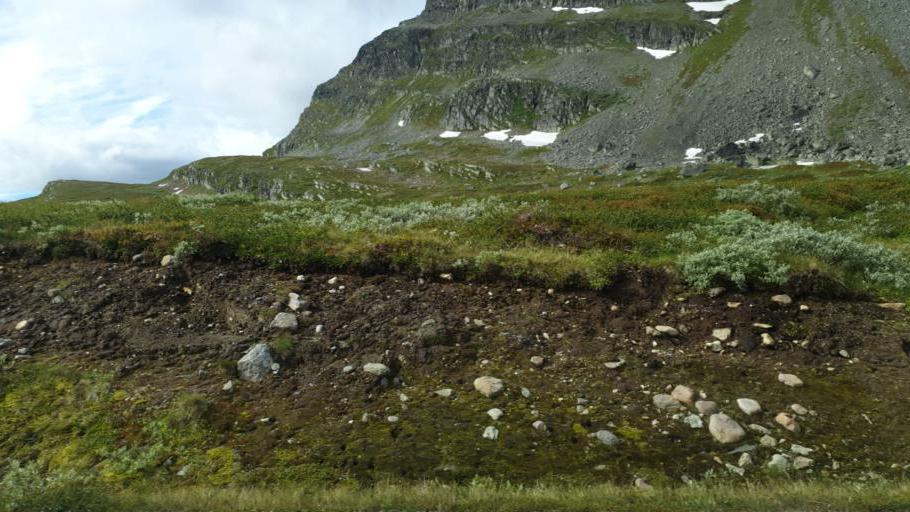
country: NO
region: Oppland
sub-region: Vestre Slidre
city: Slidre
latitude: 61.2989
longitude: 8.8130
